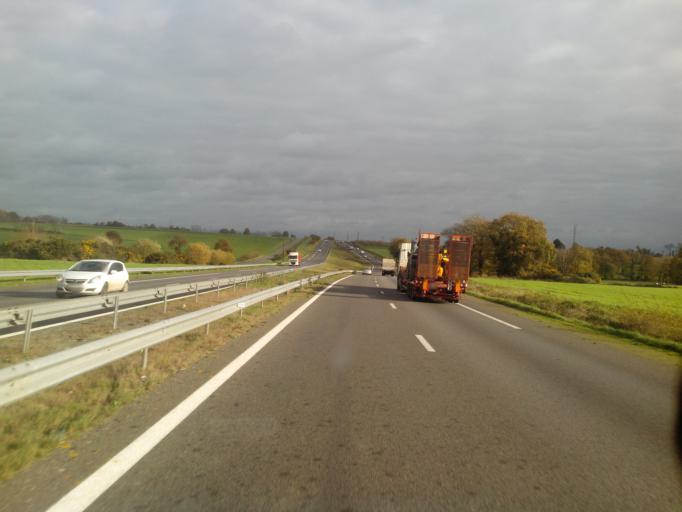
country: FR
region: Brittany
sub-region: Departement d'Ille-et-Vilaine
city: Bedee
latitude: 48.1859
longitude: -1.9836
